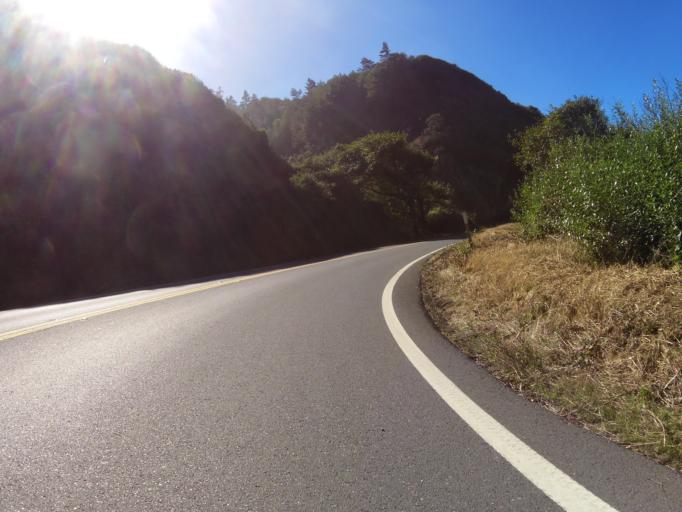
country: US
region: California
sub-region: Mendocino County
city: Fort Bragg
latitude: 39.6124
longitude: -123.7782
